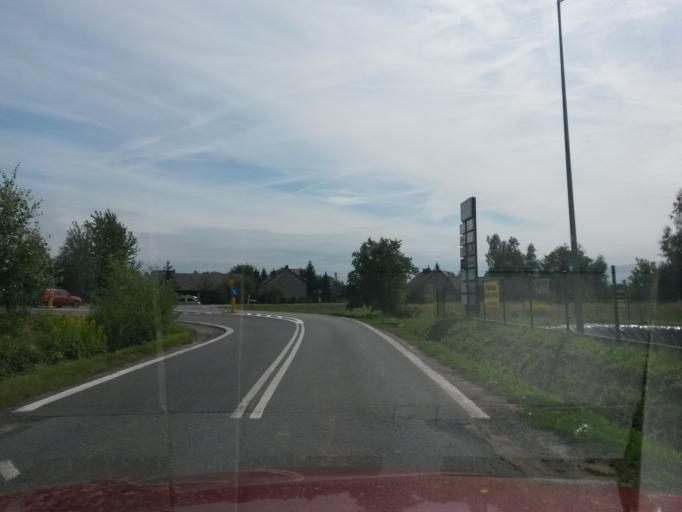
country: PL
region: Lesser Poland Voivodeship
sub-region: Powiat wielicki
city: Targowisko
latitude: 49.9826
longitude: 20.2862
